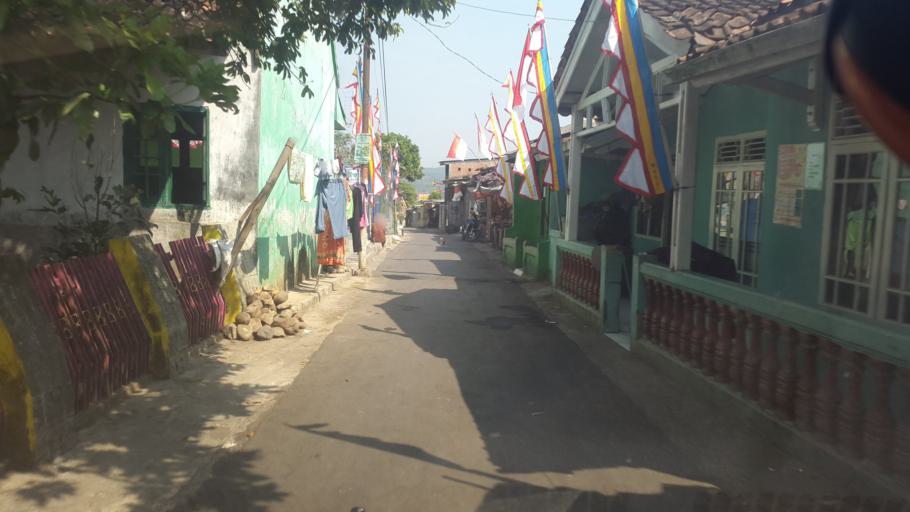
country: ID
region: West Java
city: Gunungkalong
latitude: -6.8911
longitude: 106.7851
